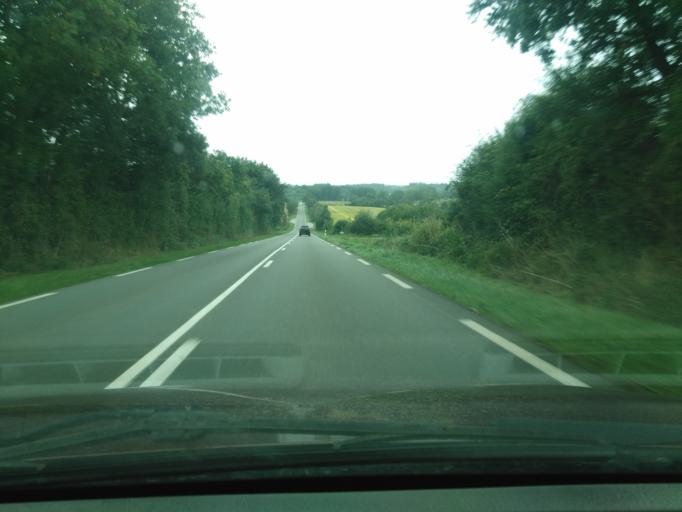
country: FR
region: Pays de la Loire
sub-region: Departement de la Vendee
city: Sainte-Hermine
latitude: 46.5735
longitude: -1.0954
